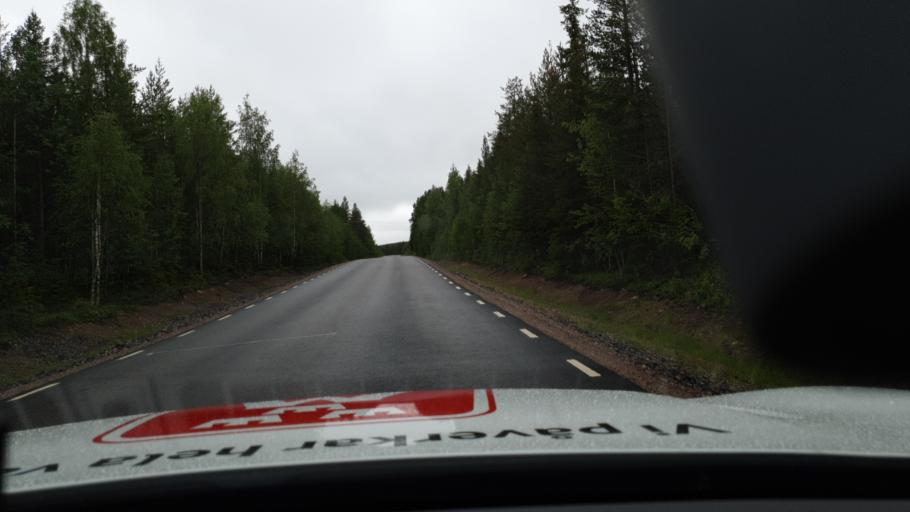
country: SE
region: Norrbotten
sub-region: Overtornea Kommun
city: OEvertornea
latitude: 66.4274
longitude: 23.5302
